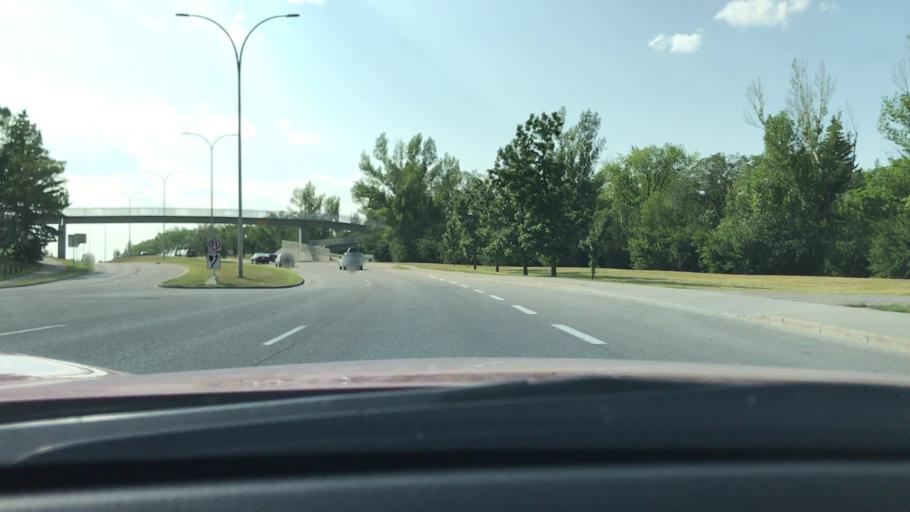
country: CA
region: Alberta
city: Calgary
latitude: 51.0246
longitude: -114.1208
